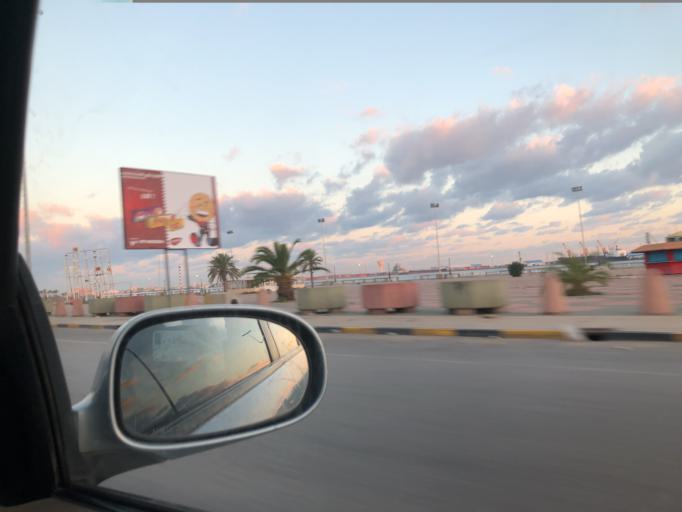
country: LY
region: Tripoli
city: Tripoli
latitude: 32.8946
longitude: 13.1891
